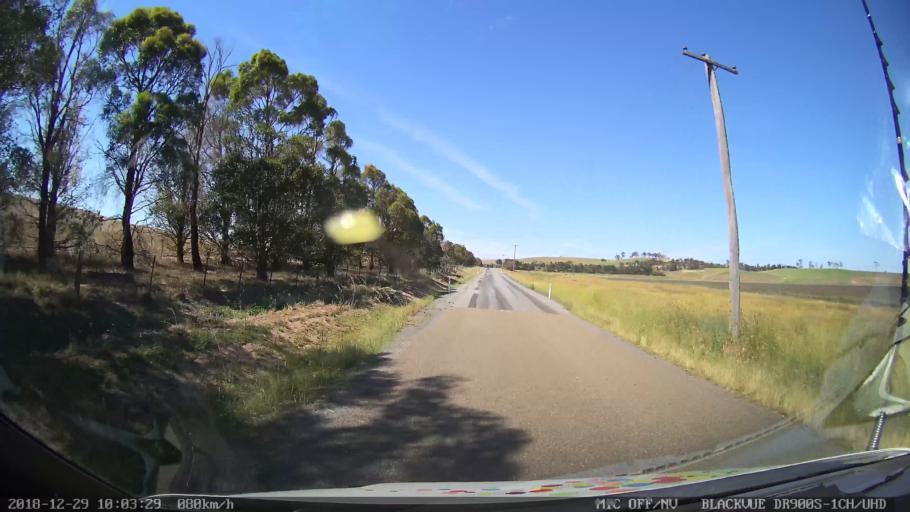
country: AU
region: New South Wales
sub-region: Goulburn Mulwaree
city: Goulburn
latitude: -34.8116
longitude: 149.4594
